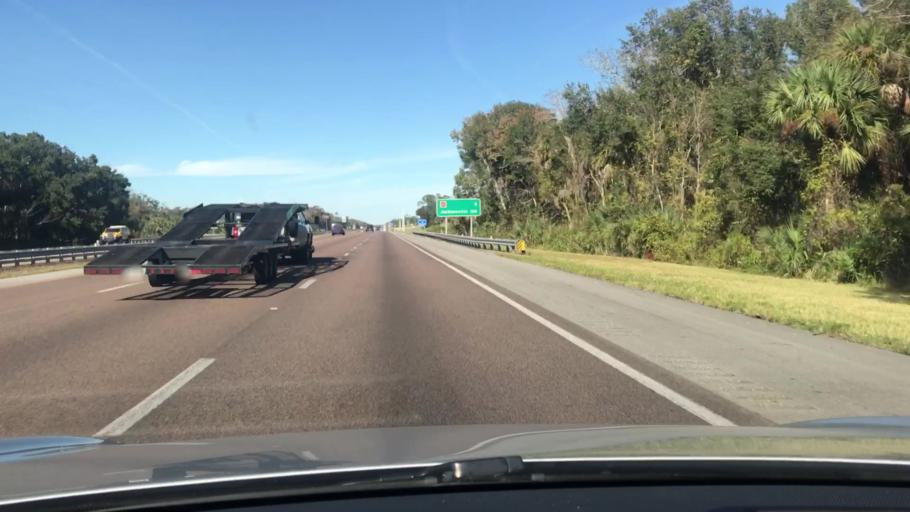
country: US
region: Florida
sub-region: Brevard County
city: Mims
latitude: 28.6786
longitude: -80.8745
